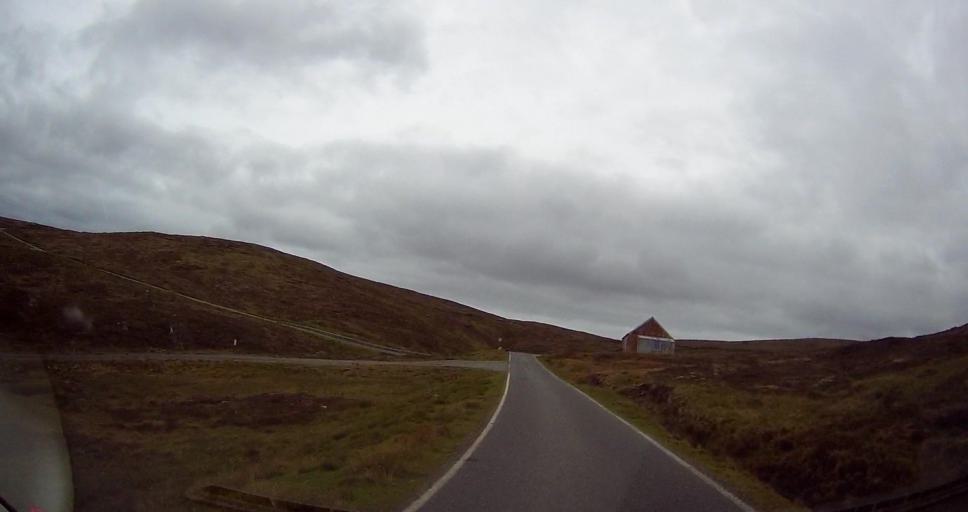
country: GB
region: Scotland
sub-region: Shetland Islands
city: Shetland
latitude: 60.5505
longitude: -1.0609
